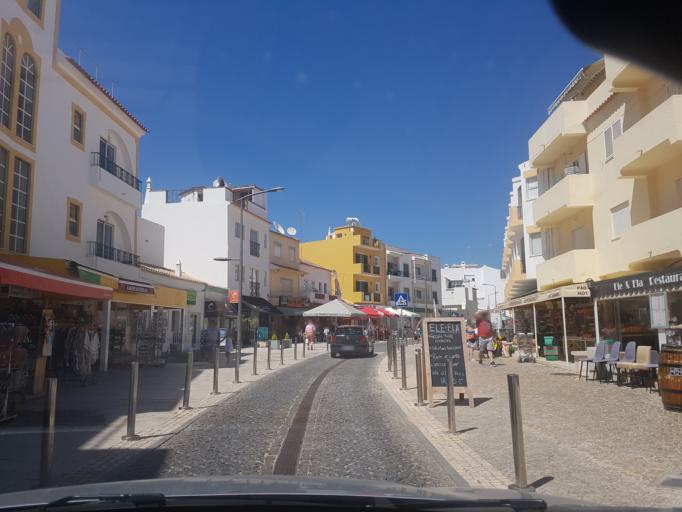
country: PT
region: Faro
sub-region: Lagoa
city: Carvoeiro
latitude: 37.0978
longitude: -8.4709
